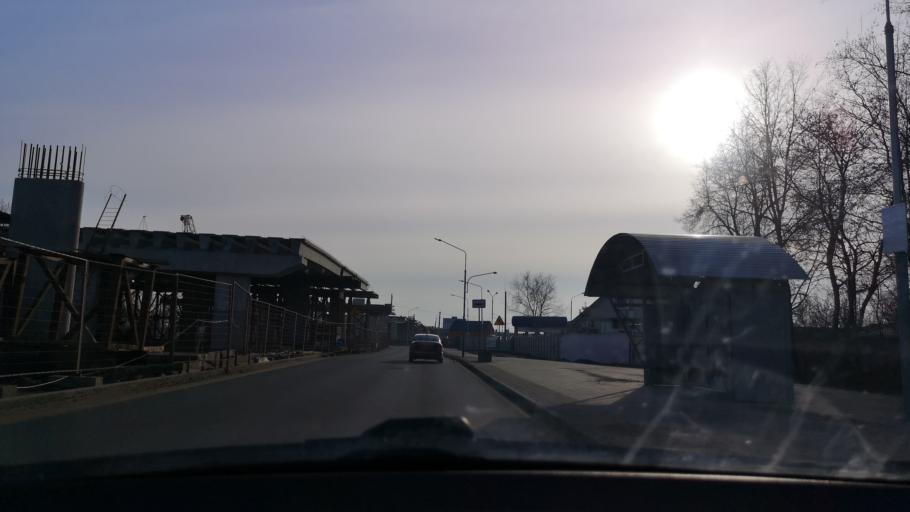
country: BY
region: Brest
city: Brest
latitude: 52.1090
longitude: 23.6668
